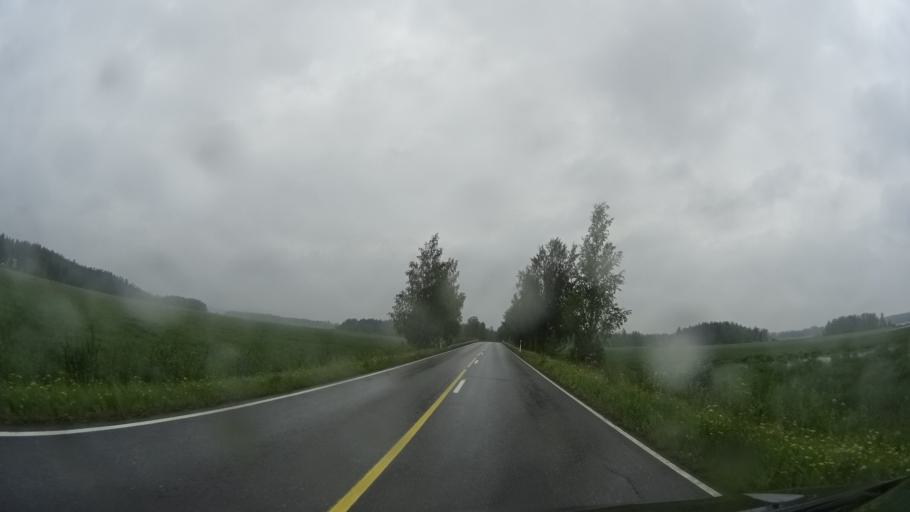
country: FI
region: North Karelia
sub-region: Keski-Karjala
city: Raeaekkylae
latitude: 62.3064
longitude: 29.5396
